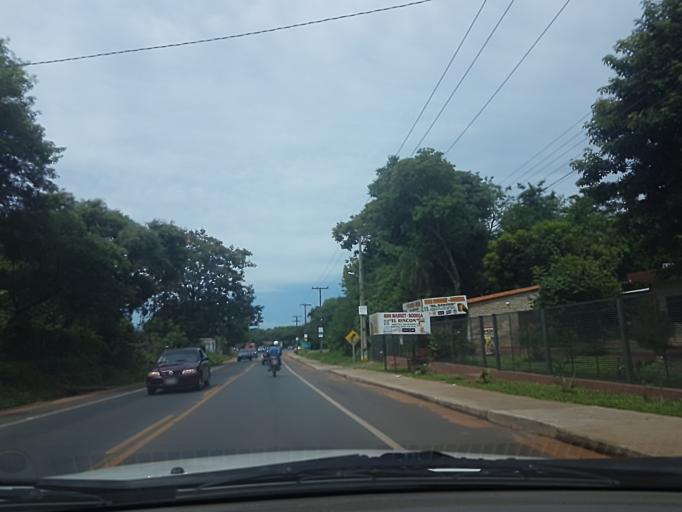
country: PY
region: Central
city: Limpio
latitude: -25.2368
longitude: -57.4520
